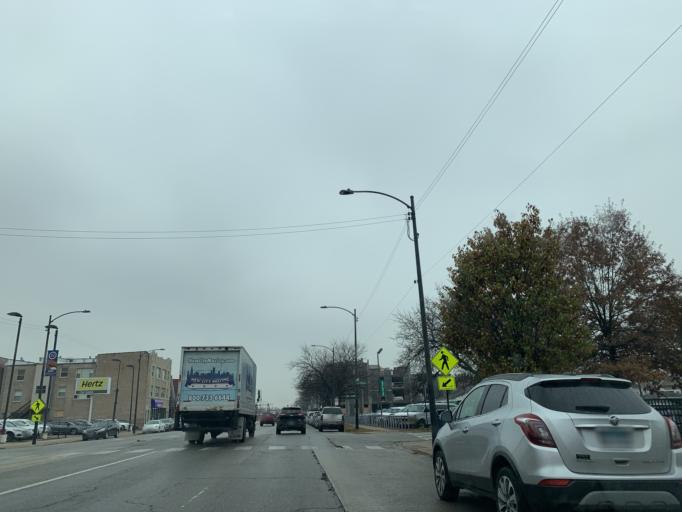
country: US
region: Illinois
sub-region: Cook County
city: Lincolnwood
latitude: 41.9525
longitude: -87.6885
